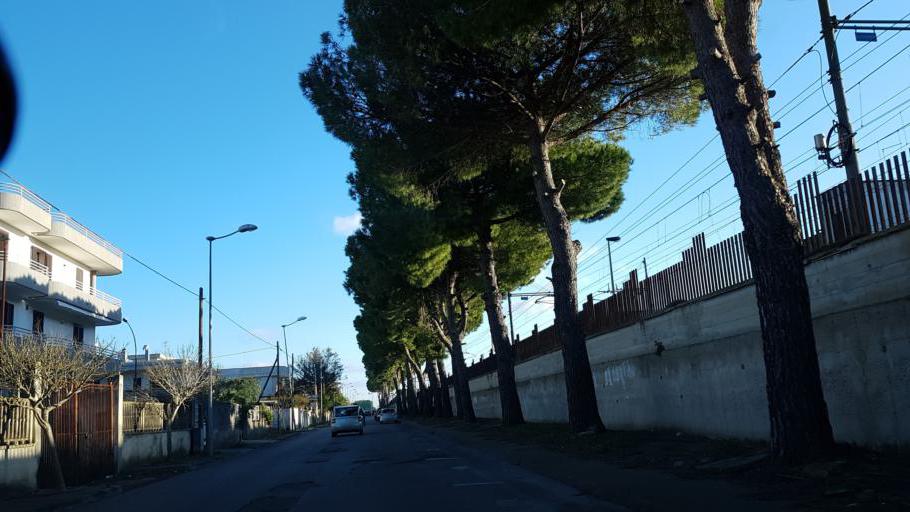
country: IT
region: Apulia
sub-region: Provincia di Lecce
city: Squinzano
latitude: 40.4366
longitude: 18.0491
